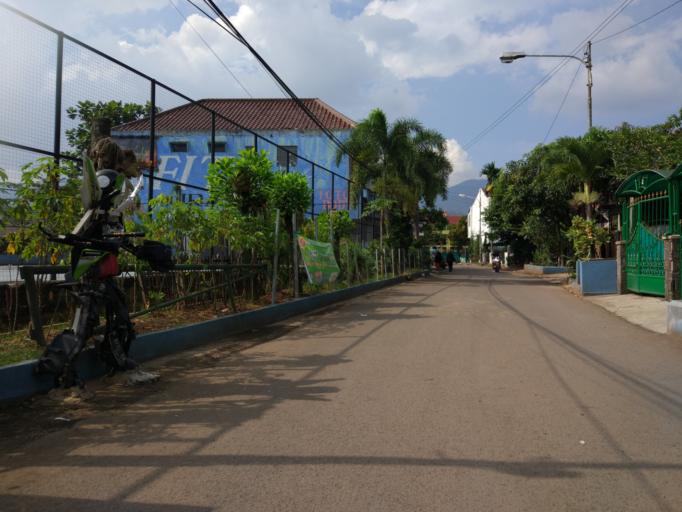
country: ID
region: West Java
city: Cileunyi
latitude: -6.9101
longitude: 107.6919
